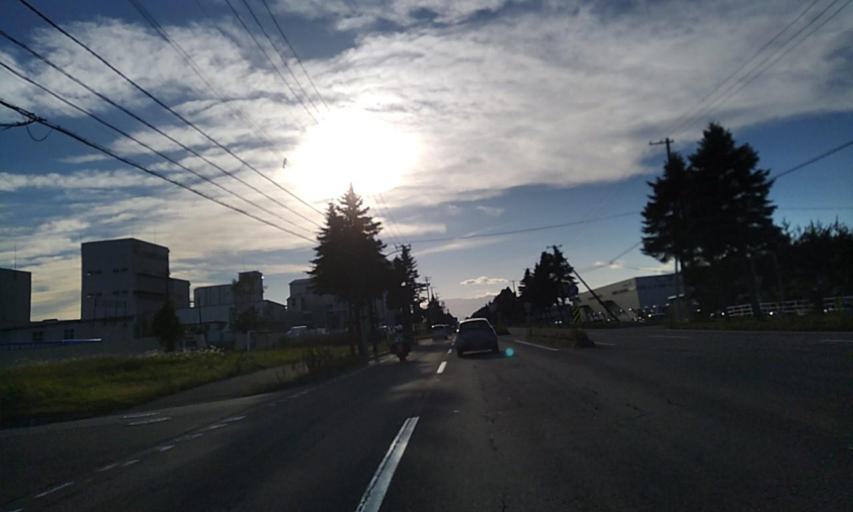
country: JP
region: Hokkaido
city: Obihiro
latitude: 42.9274
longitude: 143.1370
